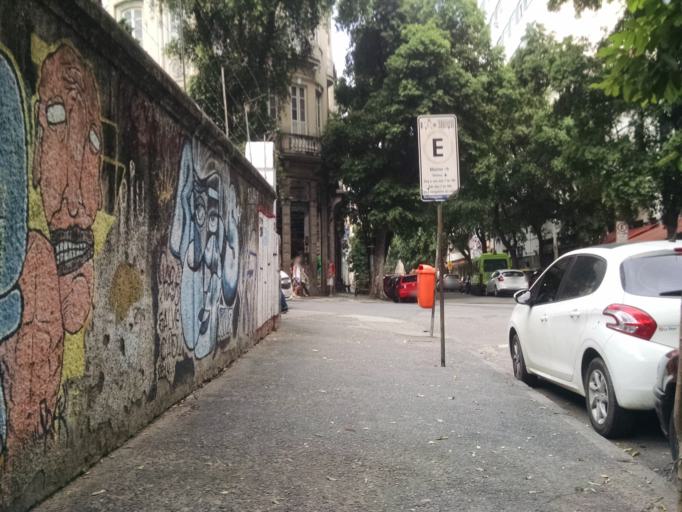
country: BR
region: Rio de Janeiro
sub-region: Rio De Janeiro
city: Rio de Janeiro
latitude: -22.9110
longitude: -43.1881
